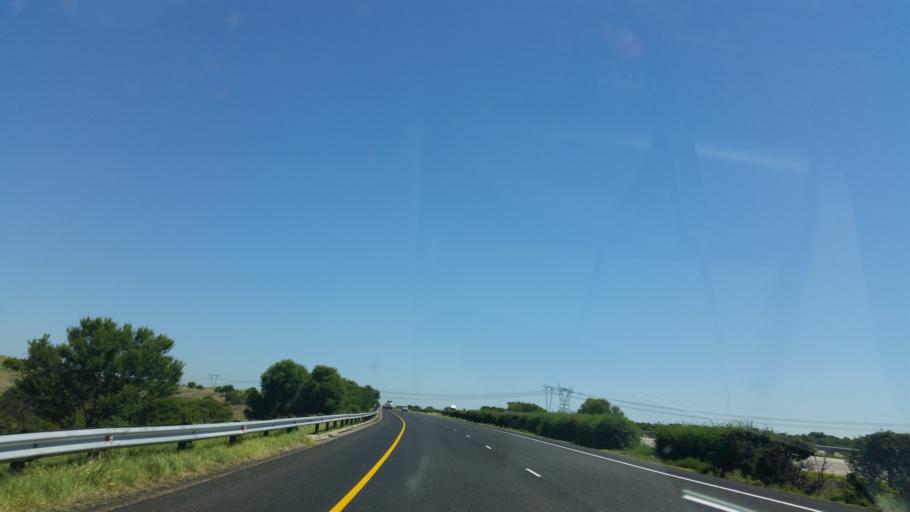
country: ZA
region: KwaZulu-Natal
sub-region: uThukela District Municipality
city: Ladysmith
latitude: -28.6670
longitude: 29.6338
